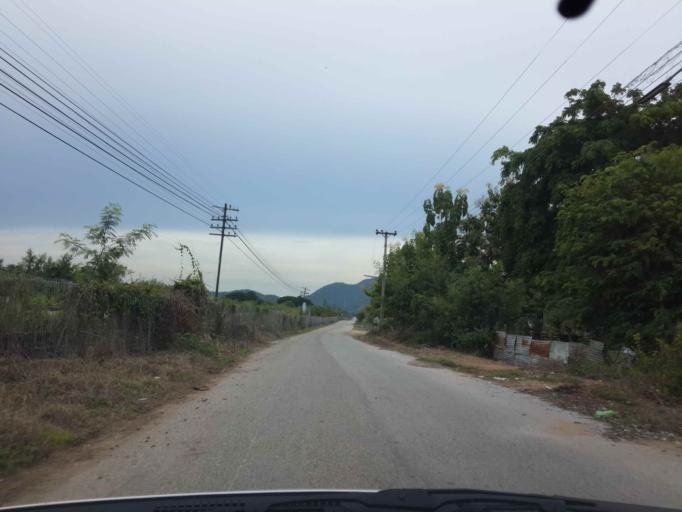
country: TH
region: Chon Buri
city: Si Racha
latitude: 13.2320
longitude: 100.9532
